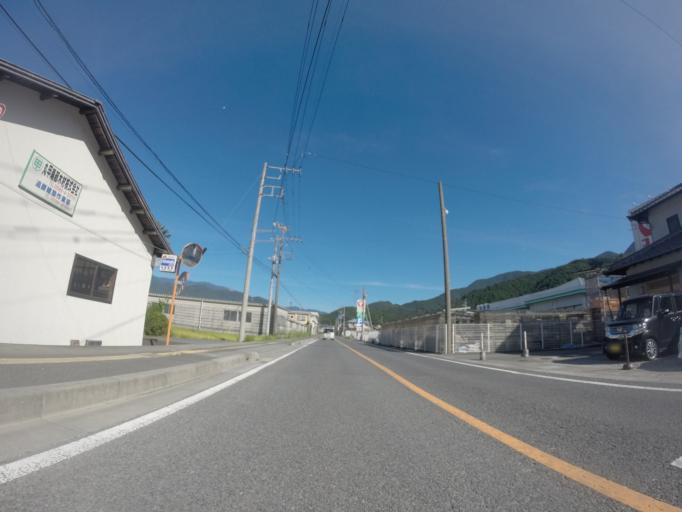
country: JP
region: Shizuoka
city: Fujinomiya
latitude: 35.2765
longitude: 138.4675
